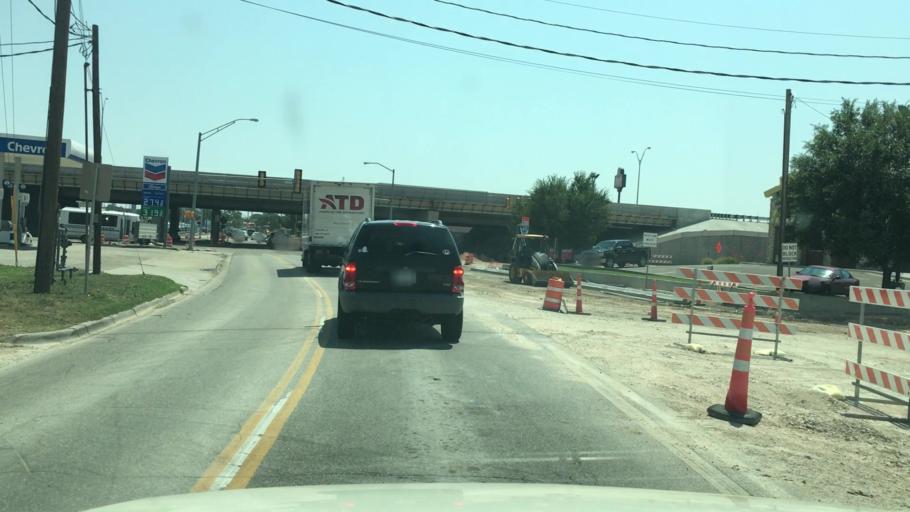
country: US
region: Texas
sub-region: Potter County
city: Amarillo
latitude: 35.1938
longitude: -101.8174
